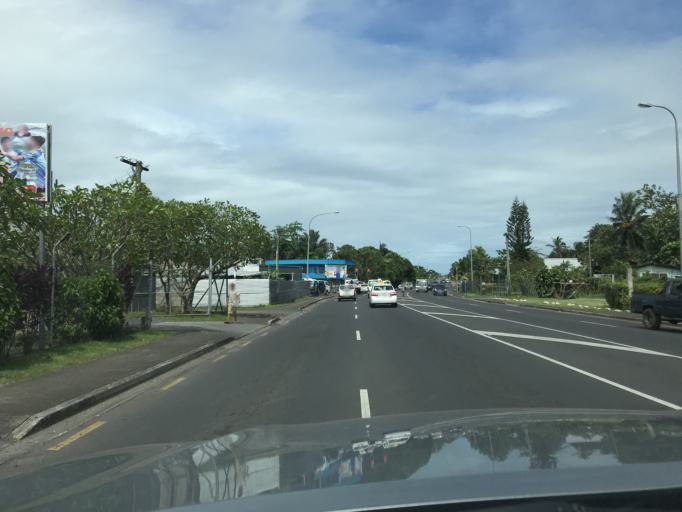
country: WS
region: Tuamasaga
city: Apia
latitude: -13.8384
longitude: -171.7725
